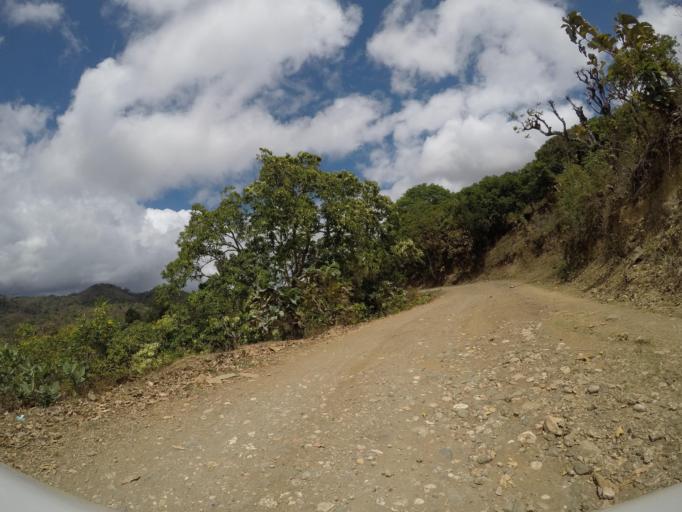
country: TL
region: Lautem
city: Lospalos
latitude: -8.5414
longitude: 126.8376
